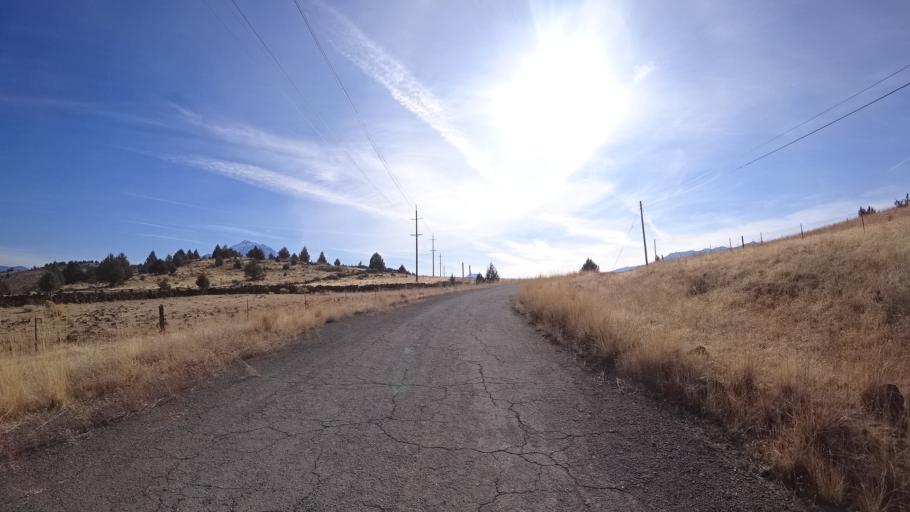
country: US
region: California
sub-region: Siskiyou County
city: Weed
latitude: 41.4985
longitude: -122.4553
